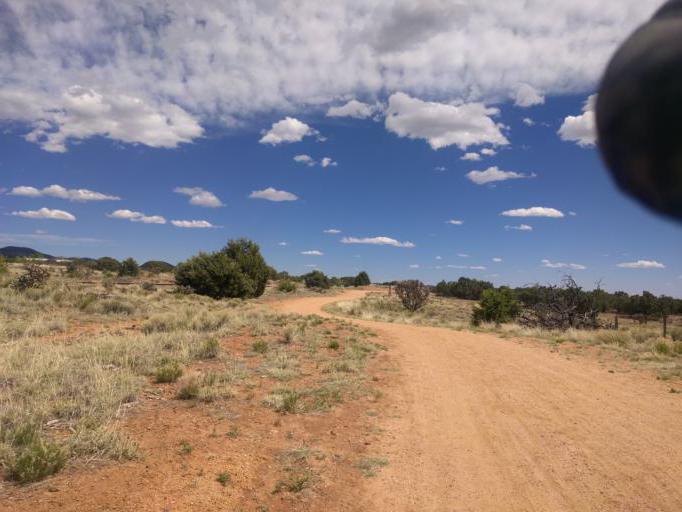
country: US
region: New Mexico
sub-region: Santa Fe County
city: Agua Fria
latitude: 35.6102
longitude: -105.9616
